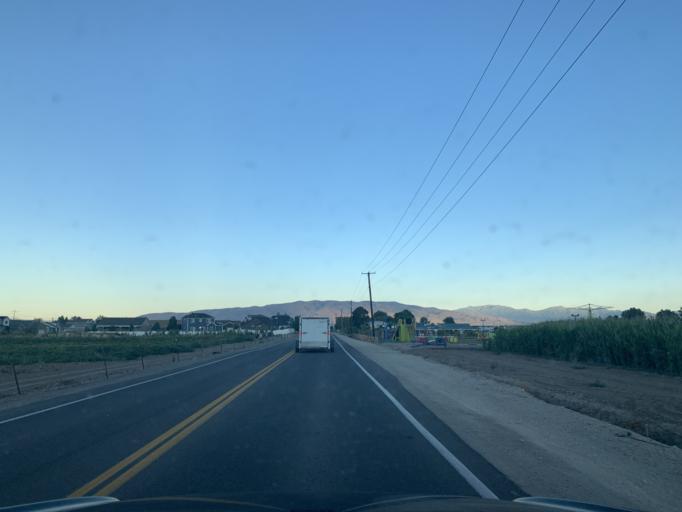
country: US
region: Utah
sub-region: Utah County
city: Orem
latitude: 40.2608
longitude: -111.7103
